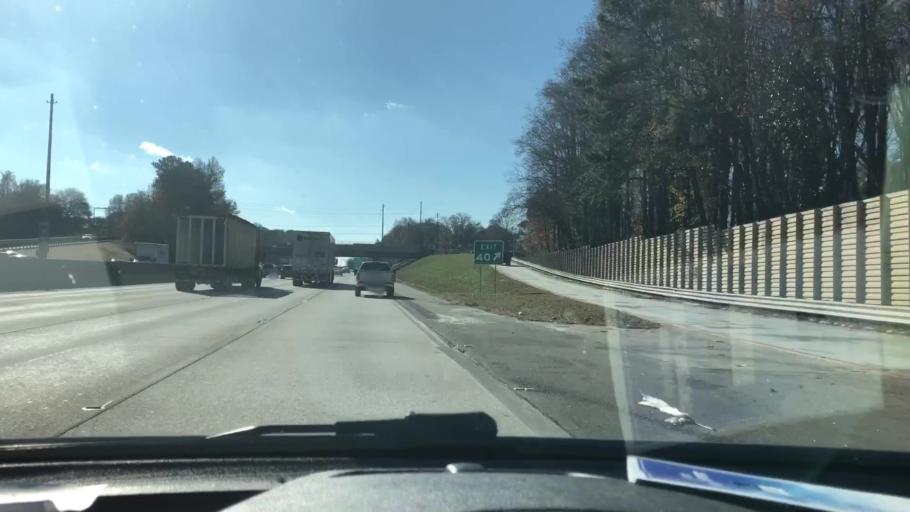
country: US
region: Georgia
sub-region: DeKalb County
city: Clarkston
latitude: 33.8057
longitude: -84.2506
